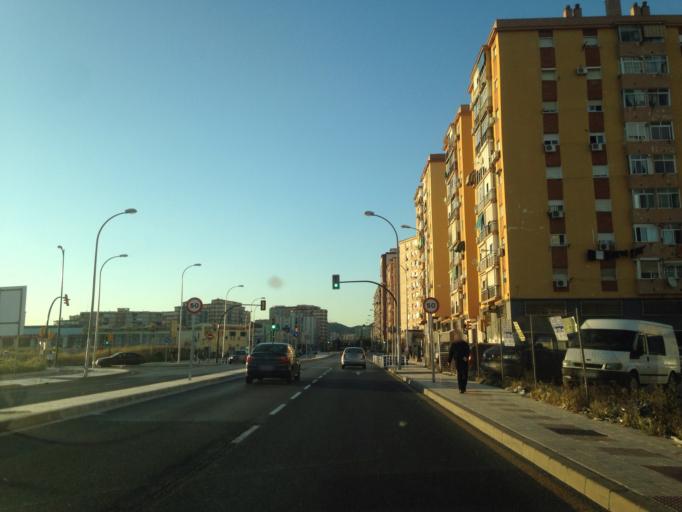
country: ES
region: Andalusia
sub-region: Provincia de Malaga
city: Malaga
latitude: 36.7065
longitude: -4.4426
